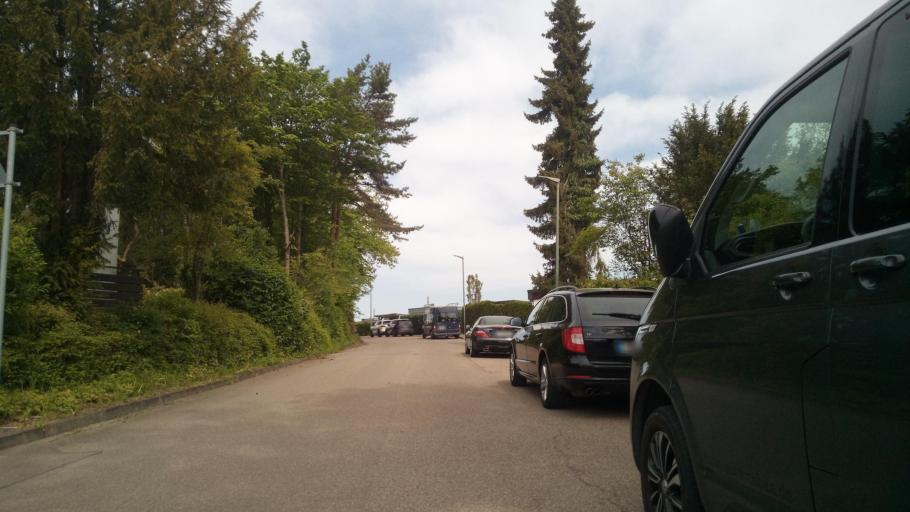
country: DE
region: Baden-Wuerttemberg
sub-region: Regierungsbezirk Stuttgart
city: Eislingen
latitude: 48.7067
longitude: 9.7077
